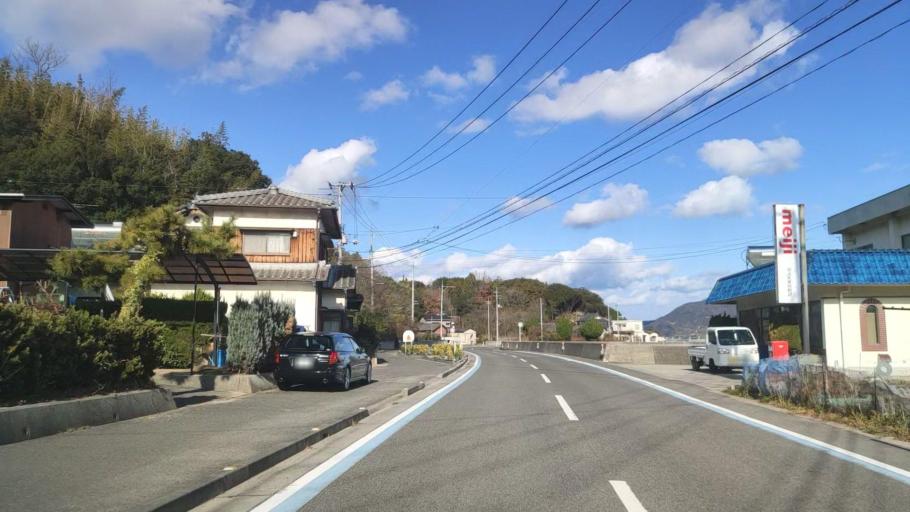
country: JP
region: Hiroshima
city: Innoshima
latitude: 34.2208
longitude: 133.1070
